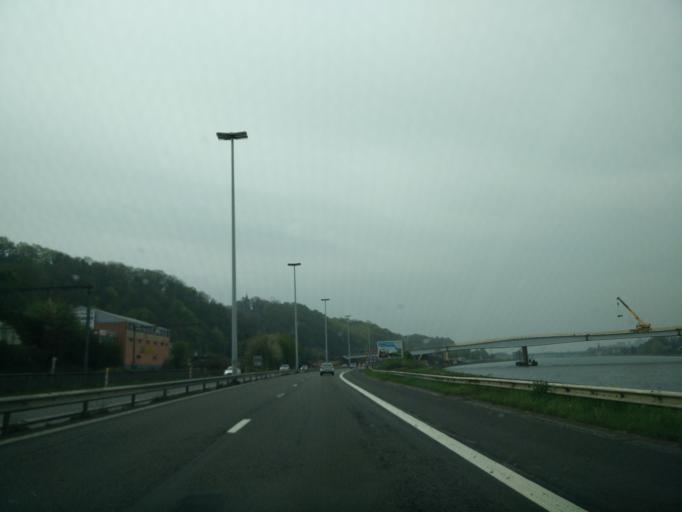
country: BE
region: Wallonia
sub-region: Province de Liege
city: Vise
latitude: 50.7221
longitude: 5.6922
